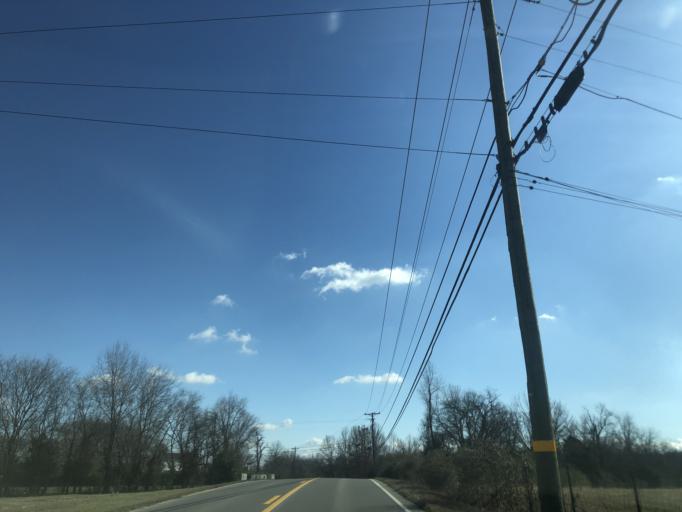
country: US
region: Tennessee
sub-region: Rutherford County
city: Murfreesboro
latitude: 35.9650
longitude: -86.3922
